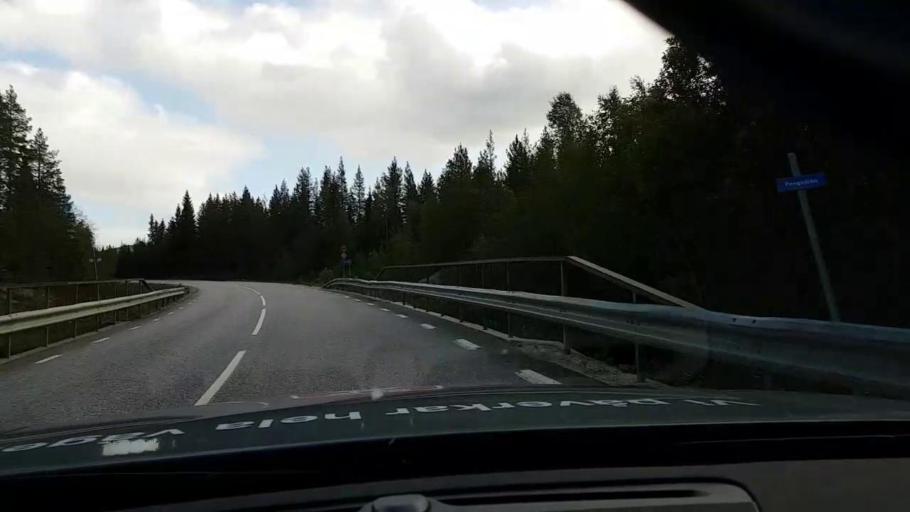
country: SE
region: Vaesternorrland
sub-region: OErnskoeldsviks Kommun
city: Bredbyn
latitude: 63.6868
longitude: 17.7710
